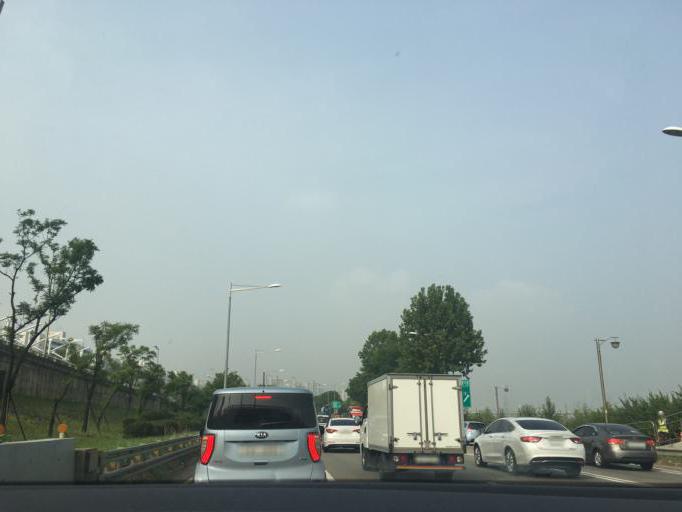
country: KR
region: Gyeonggi-do
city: Guri-si
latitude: 37.5235
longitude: 127.1020
